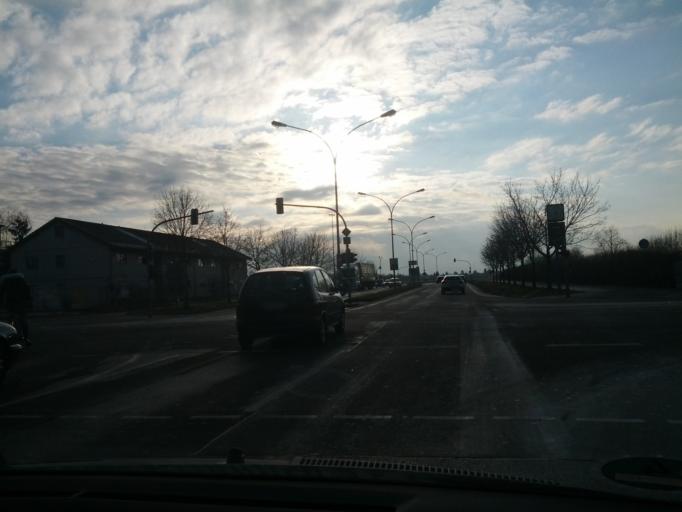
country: DE
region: Baden-Wuerttemberg
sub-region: Freiburg Region
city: Freiburg
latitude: 48.0189
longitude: 7.8412
